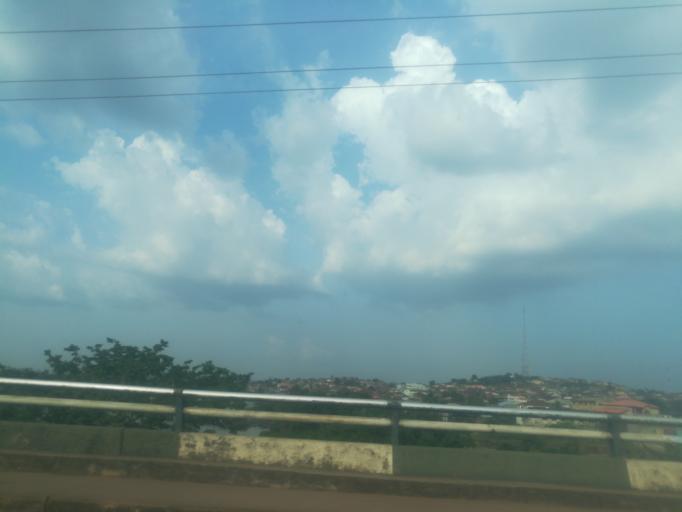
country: NG
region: Ogun
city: Abeokuta
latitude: 7.1484
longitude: 3.3256
